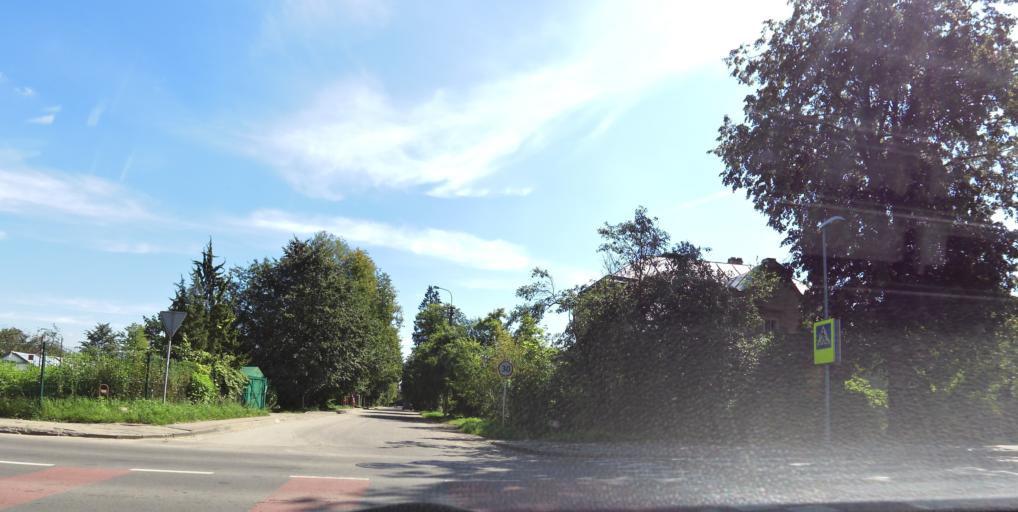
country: LT
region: Vilnius County
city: Rasos
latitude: 54.6724
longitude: 25.3619
